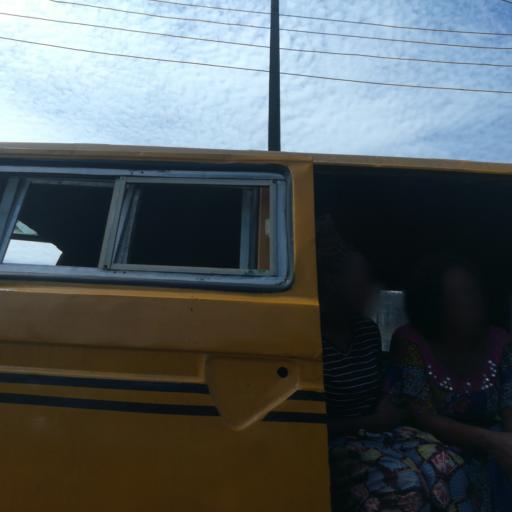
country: NG
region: Lagos
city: Lagos
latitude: 6.4623
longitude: 3.3931
